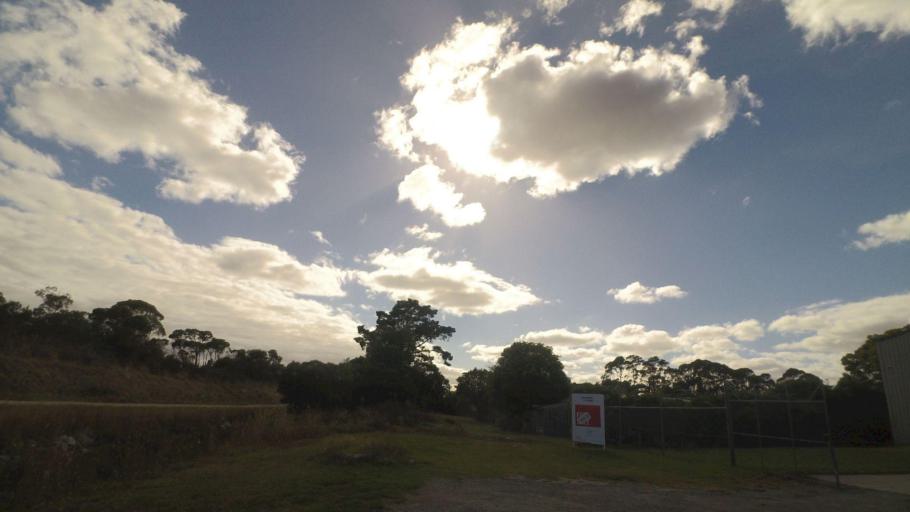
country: AU
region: Victoria
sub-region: Cardinia
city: Koo-Wee-Rup
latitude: -38.1967
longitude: 145.4818
